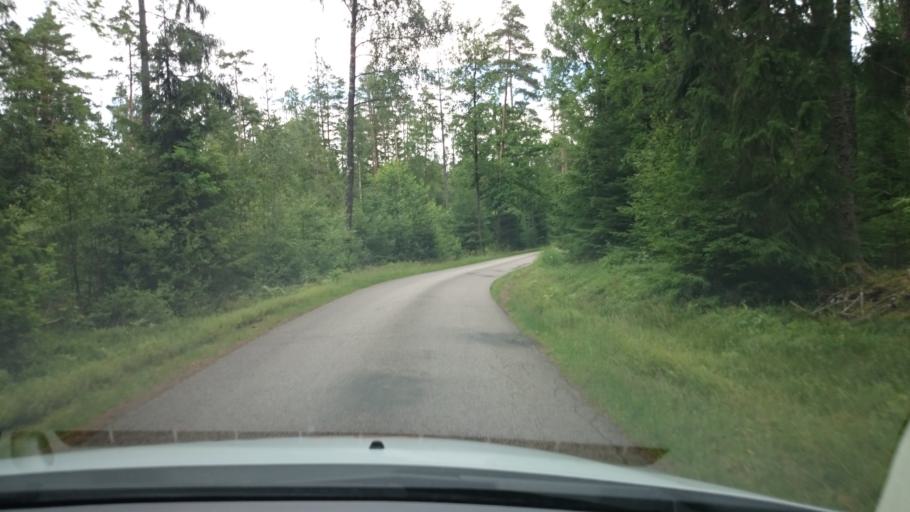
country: SE
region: Halland
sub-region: Hylte Kommun
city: Hyltebruk
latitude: 56.9596
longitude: 13.1816
